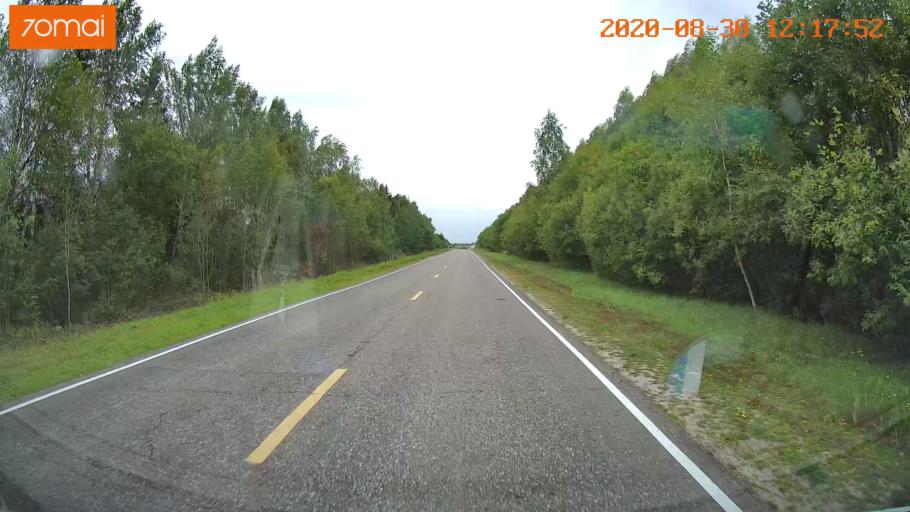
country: RU
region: Ivanovo
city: Yur'yevets
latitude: 57.3236
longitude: 42.9665
